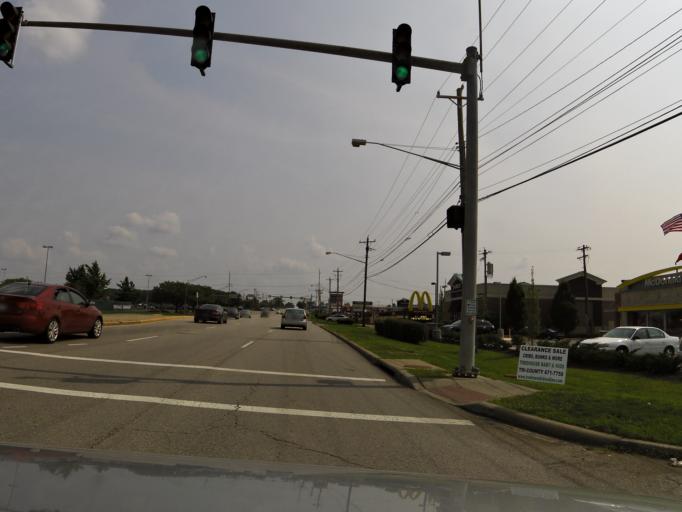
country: US
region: Ohio
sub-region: Hamilton County
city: Springdale
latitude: 39.2904
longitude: -84.4668
